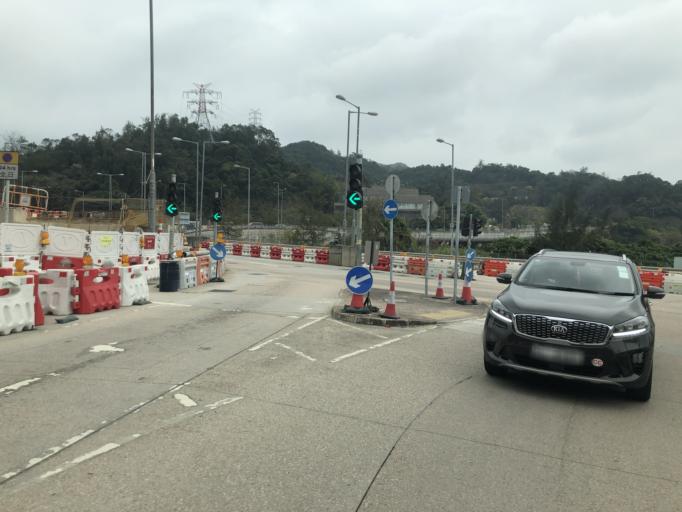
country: HK
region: Wong Tai Sin
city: Wong Tai Sin
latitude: 22.3345
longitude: 114.2269
